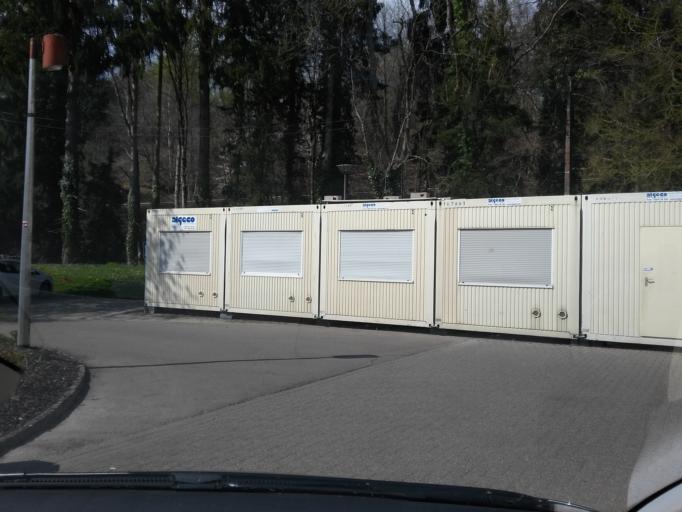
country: BE
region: Wallonia
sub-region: Province du Luxembourg
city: Habay-la-Vieille
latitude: 49.7319
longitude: 5.6539
